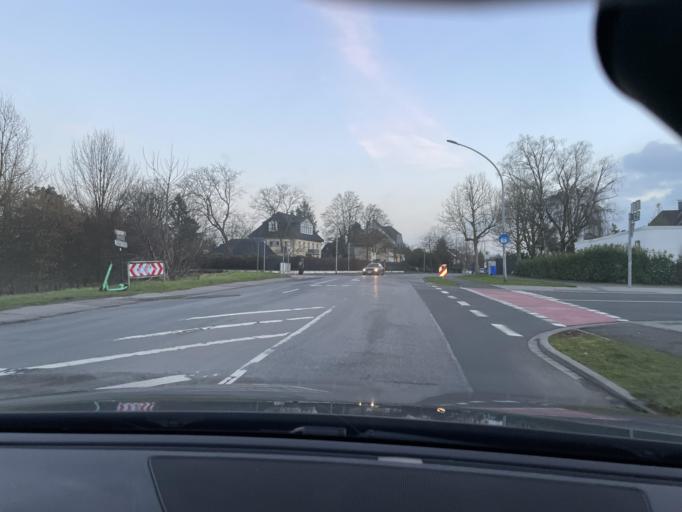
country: DE
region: North Rhine-Westphalia
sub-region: Regierungsbezirk Dusseldorf
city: Monchengladbach
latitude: 51.2161
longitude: 6.4196
